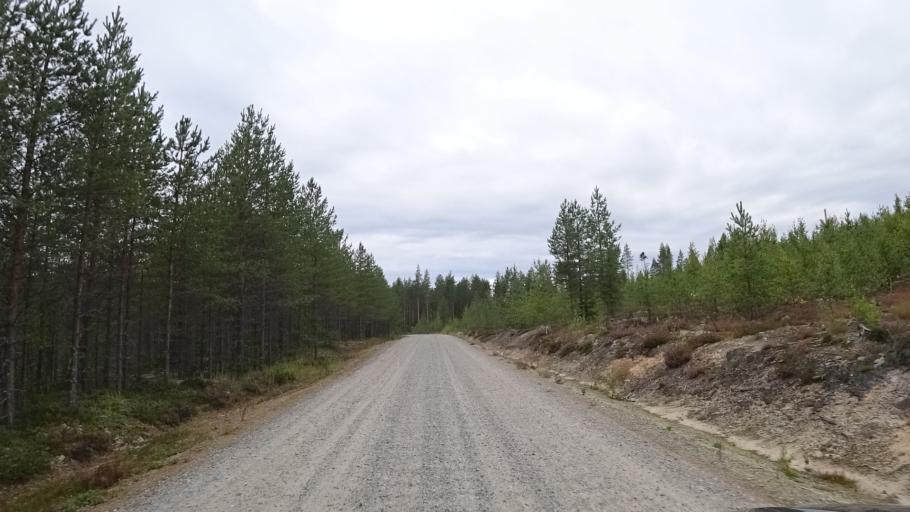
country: FI
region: North Karelia
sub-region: Joensuu
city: Ilomantsi
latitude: 63.1548
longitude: 30.6363
